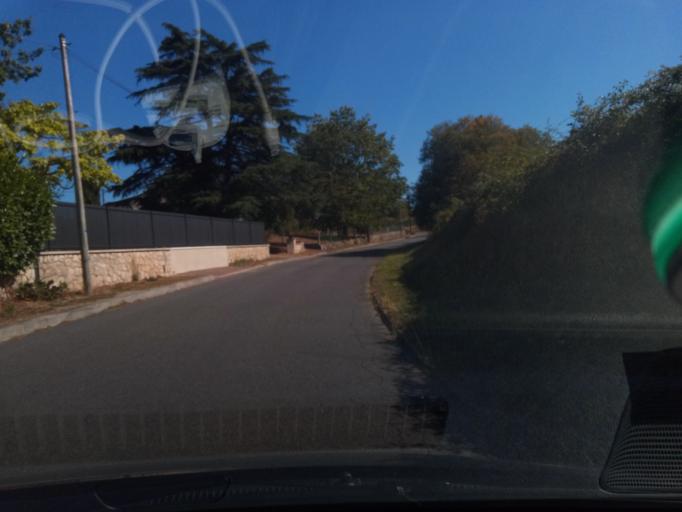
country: FR
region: Poitou-Charentes
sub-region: Departement de la Vienne
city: Saulge
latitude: 46.3800
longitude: 0.8776
